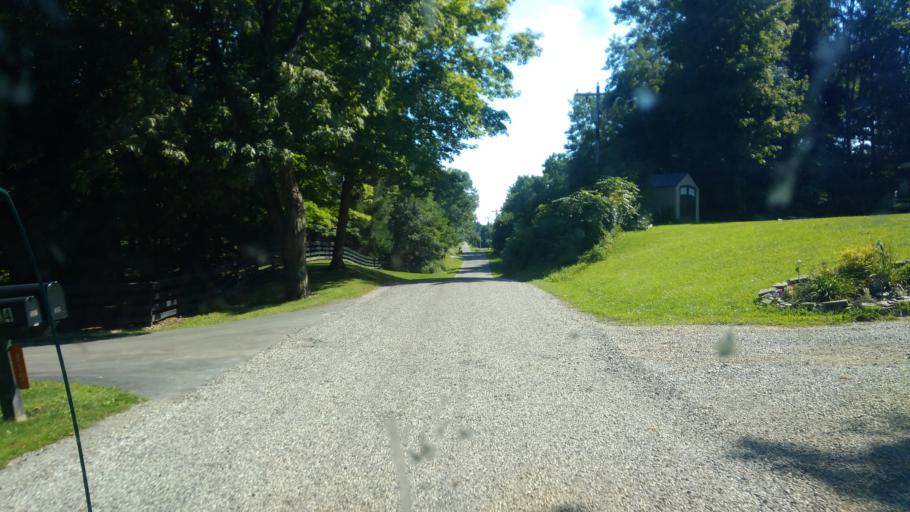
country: US
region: Ohio
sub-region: Ashland County
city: Ashland
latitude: 40.9435
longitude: -82.3397
